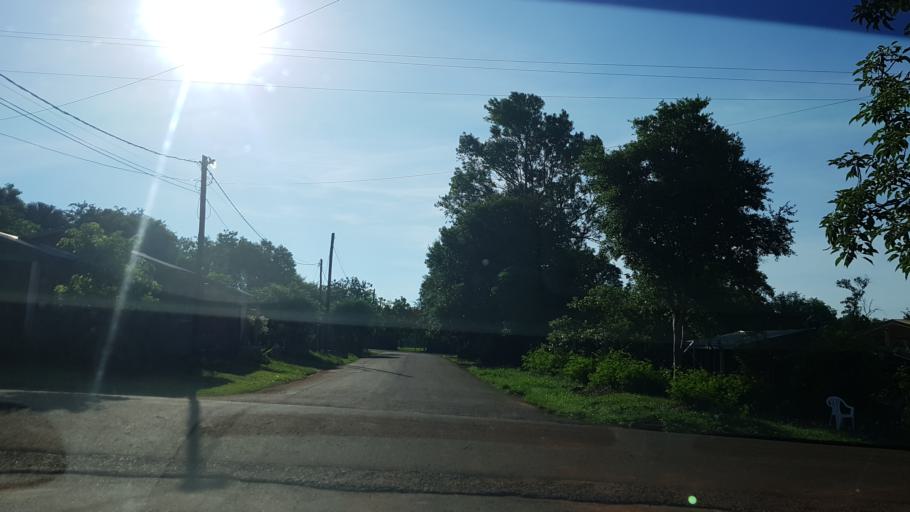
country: AR
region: Misiones
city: Puerto Libertad
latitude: -25.9228
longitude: -54.5870
